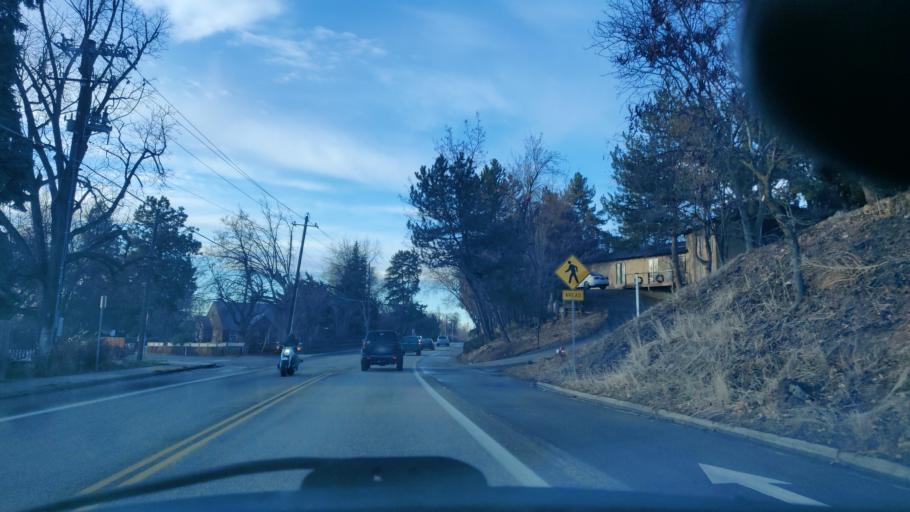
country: US
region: Idaho
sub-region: Ada County
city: Boise
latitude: 43.6424
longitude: -116.2128
